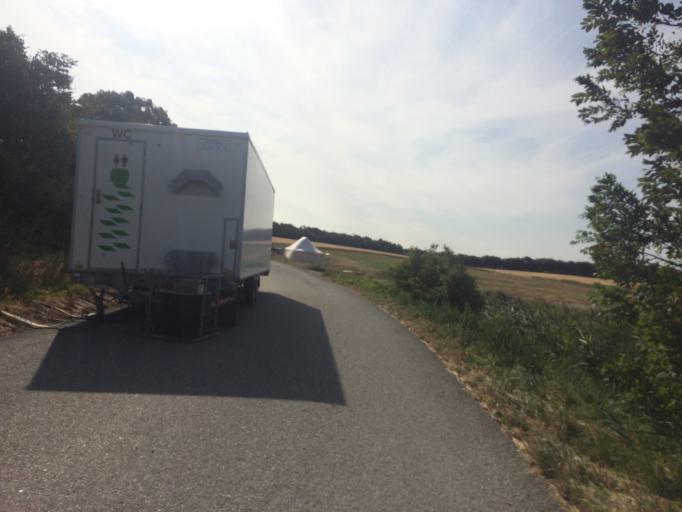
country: DK
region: Central Jutland
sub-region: Holstebro Kommune
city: Vinderup
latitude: 56.6385
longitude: 8.7814
